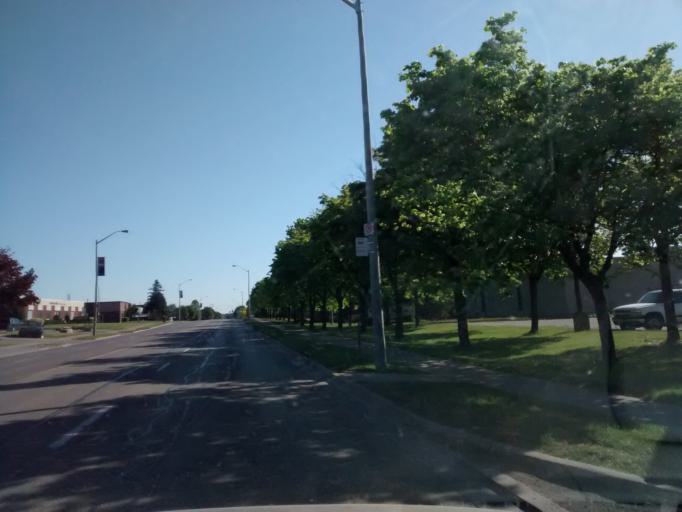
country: CA
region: Ontario
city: Burlington
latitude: 43.3588
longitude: -79.8087
